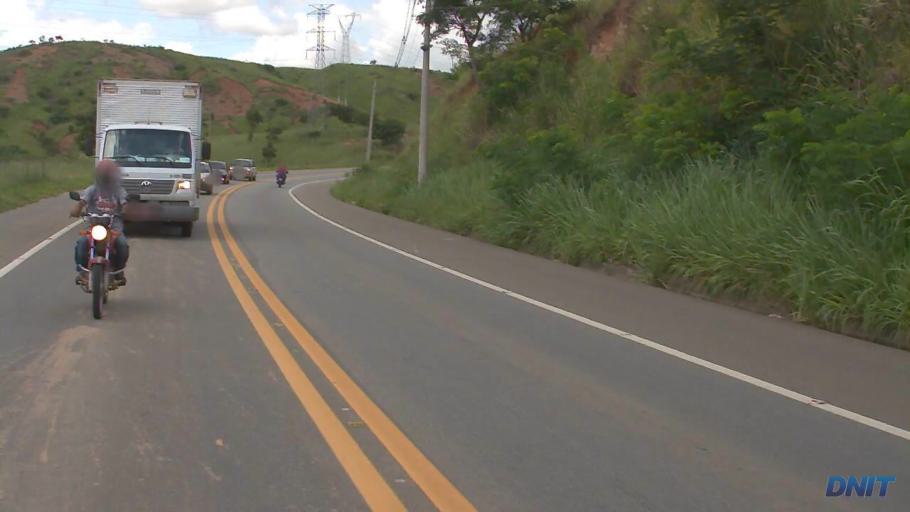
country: BR
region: Minas Gerais
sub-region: Governador Valadares
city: Governador Valadares
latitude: -18.8714
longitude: -41.9916
